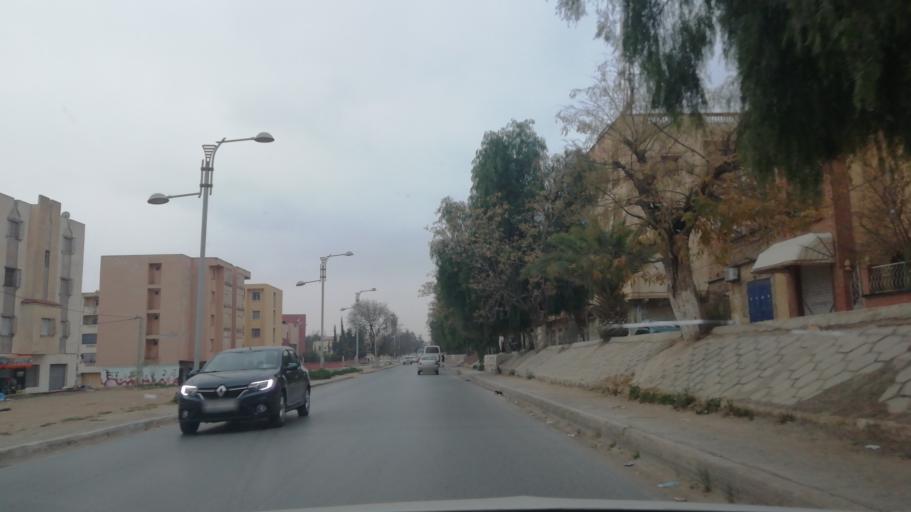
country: DZ
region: Sidi Bel Abbes
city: Sfizef
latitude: 35.2395
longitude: -0.2329
